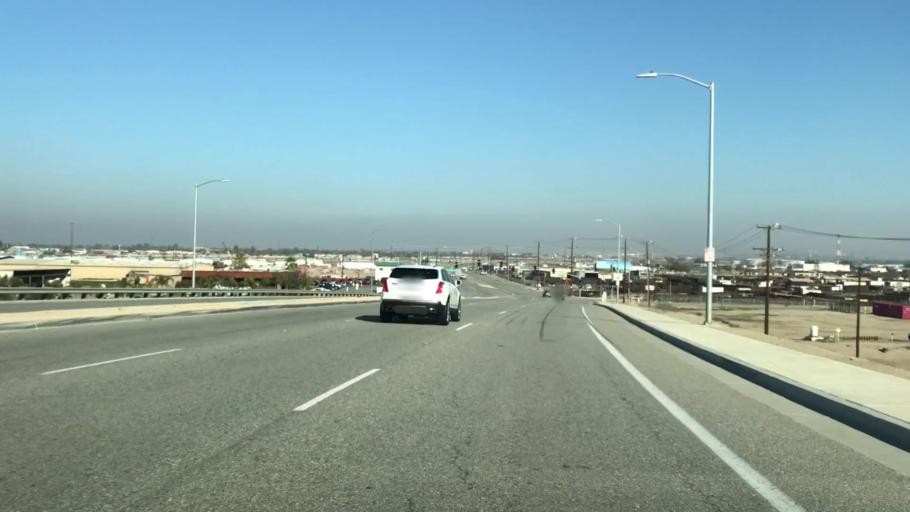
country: US
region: California
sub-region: Kern County
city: Greenacres
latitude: 35.3770
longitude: -119.0658
